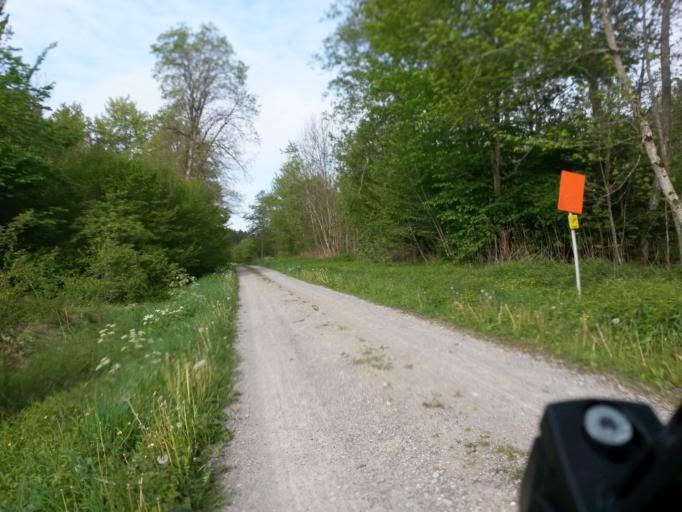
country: DE
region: Baden-Wuerttemberg
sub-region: Tuebingen Region
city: Baindt
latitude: 47.8925
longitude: 9.6715
